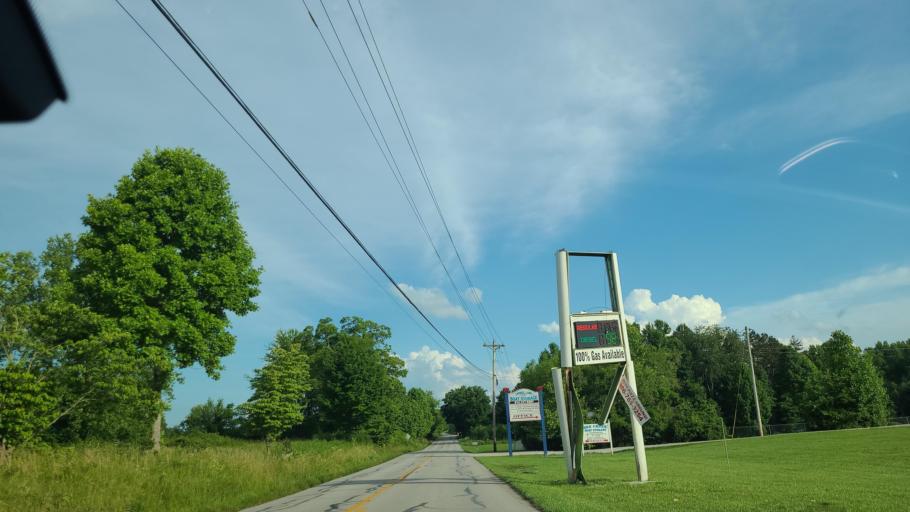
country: US
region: Kentucky
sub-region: Whitley County
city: Corbin
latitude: 36.9023
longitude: -84.2366
